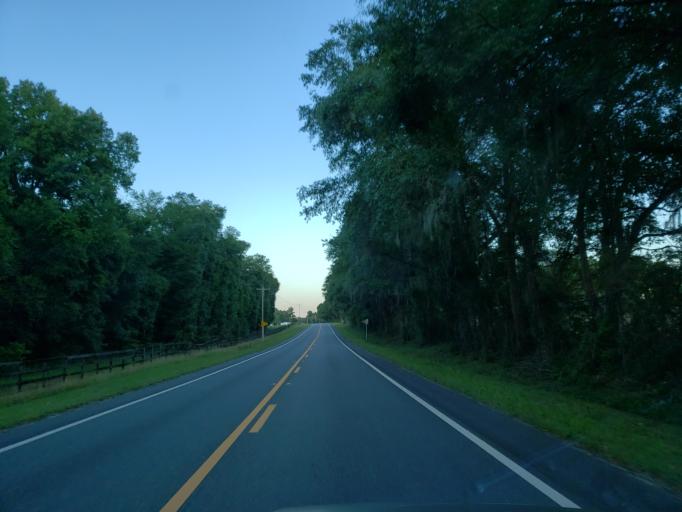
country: US
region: Georgia
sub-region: Echols County
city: Statenville
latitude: 30.5811
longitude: -83.1970
